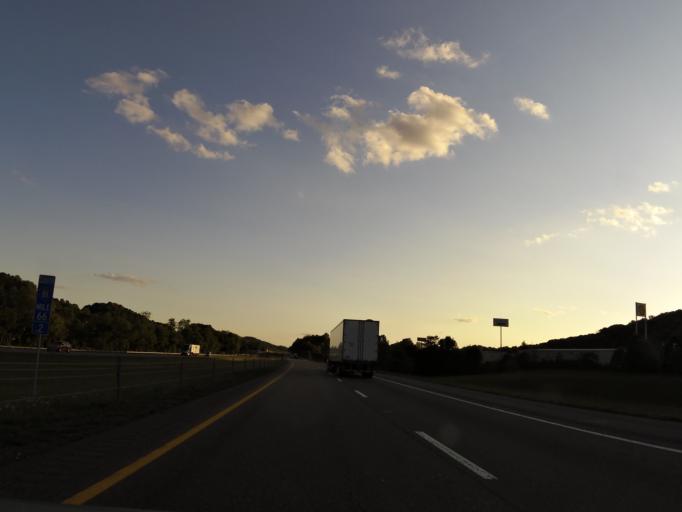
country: US
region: Tennessee
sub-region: Sullivan County
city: Blountville
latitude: 36.5334
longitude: -82.3882
